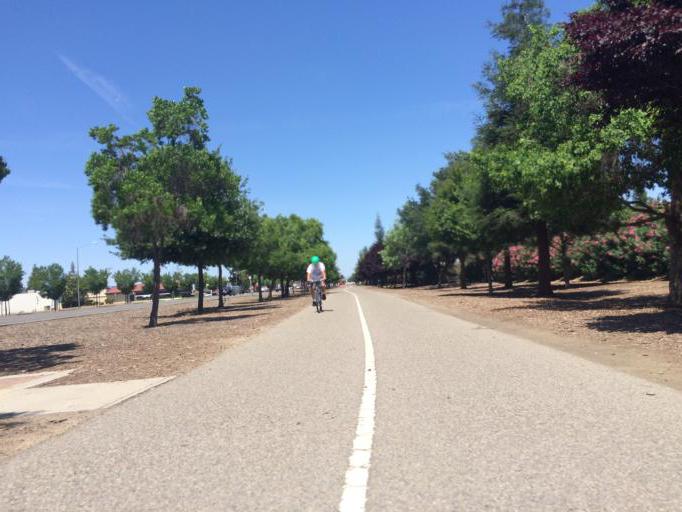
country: US
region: California
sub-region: Fresno County
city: Tarpey Village
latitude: 36.8054
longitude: -119.7001
